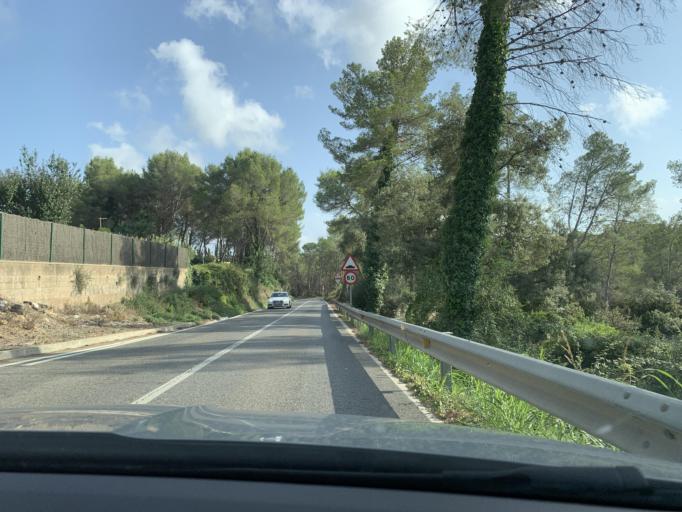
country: ES
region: Catalonia
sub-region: Provincia de Tarragona
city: el Catllar
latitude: 41.1548
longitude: 1.3141
